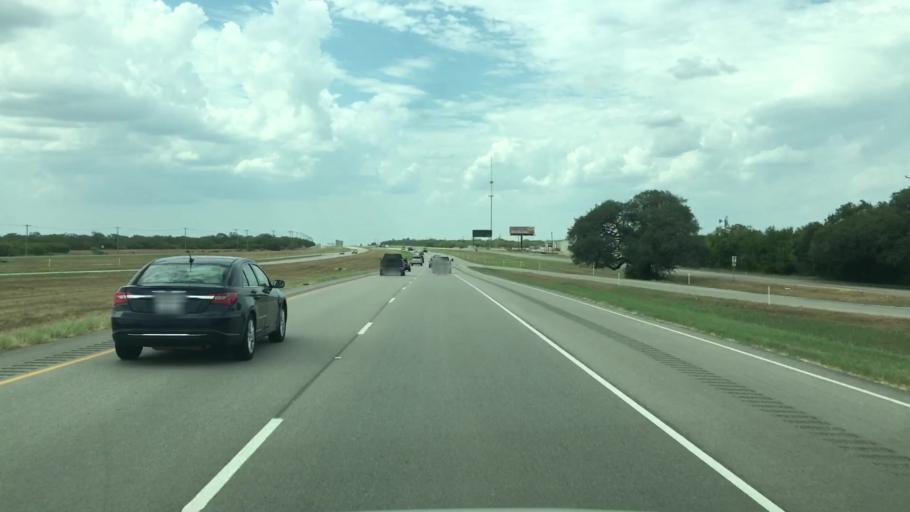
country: US
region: Texas
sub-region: Live Oak County
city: Three Rivers
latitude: 28.4910
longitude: -98.1448
